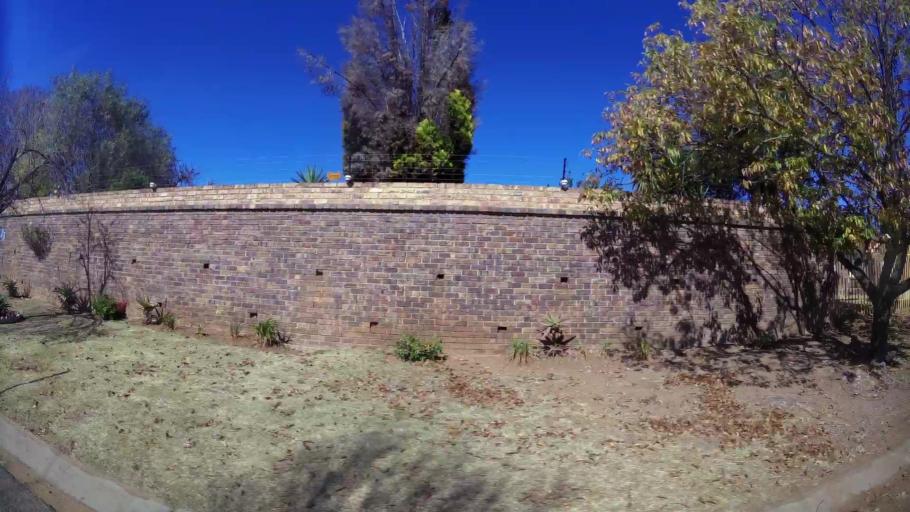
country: ZA
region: Mpumalanga
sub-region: Nkangala District Municipality
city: Witbank
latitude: -25.8582
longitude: 29.2524
